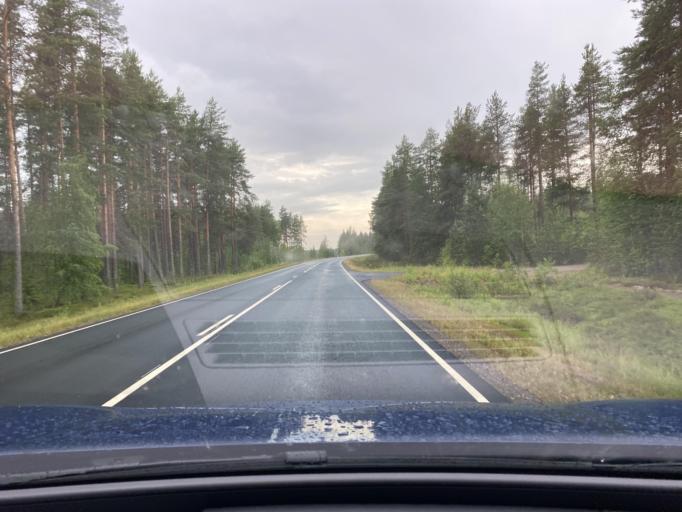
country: FI
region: Central Ostrobothnia
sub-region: Kaustinen
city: Veteli
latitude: 63.4099
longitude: 23.9649
